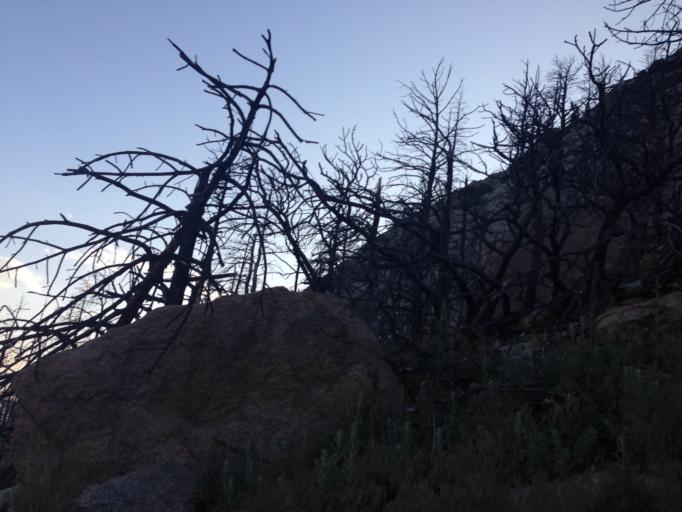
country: US
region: Colorado
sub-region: Larimer County
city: Laporte
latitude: 40.7145
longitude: -105.2913
